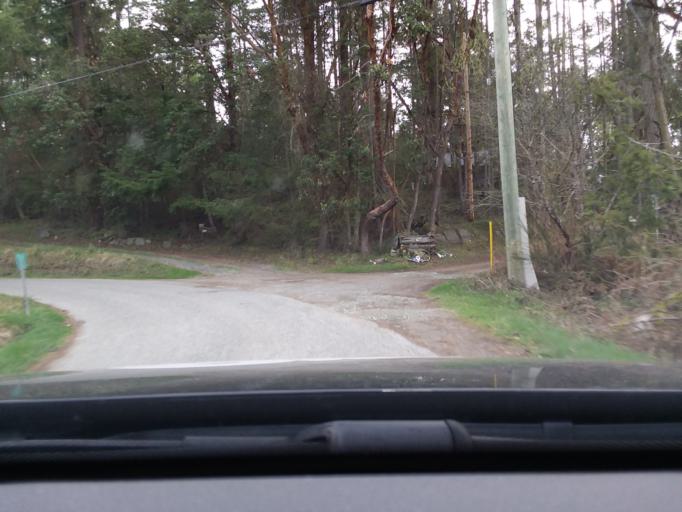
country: CA
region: British Columbia
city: North Saanich
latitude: 48.8796
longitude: -123.3141
